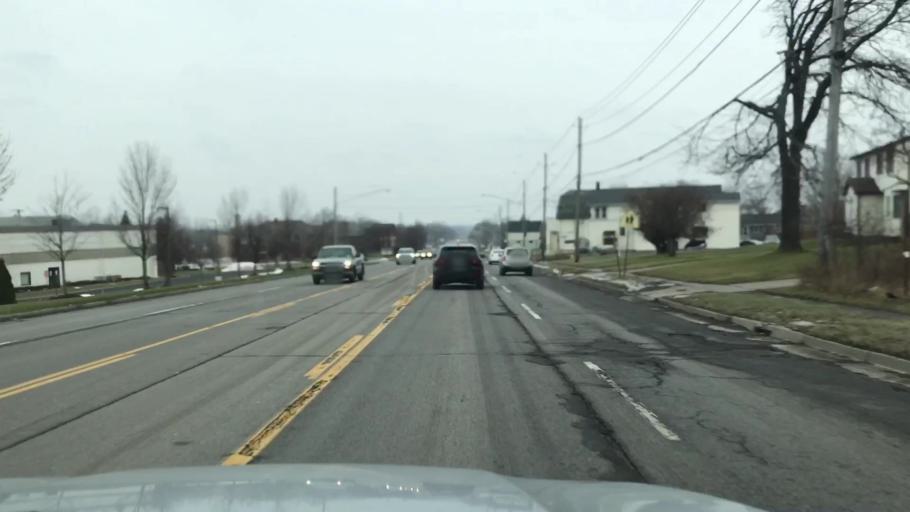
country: US
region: New York
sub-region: Erie County
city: Blasdell
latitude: 42.7977
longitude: -78.7952
